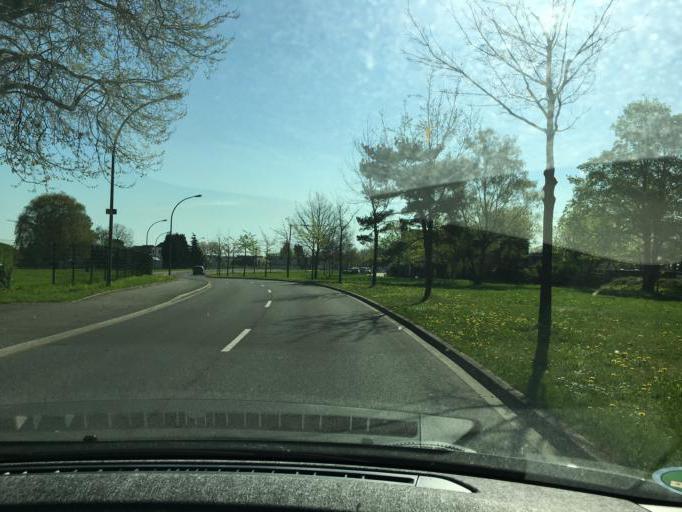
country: DE
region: North Rhine-Westphalia
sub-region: Regierungsbezirk Dusseldorf
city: Monchengladbach
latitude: 51.1746
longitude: 6.4314
